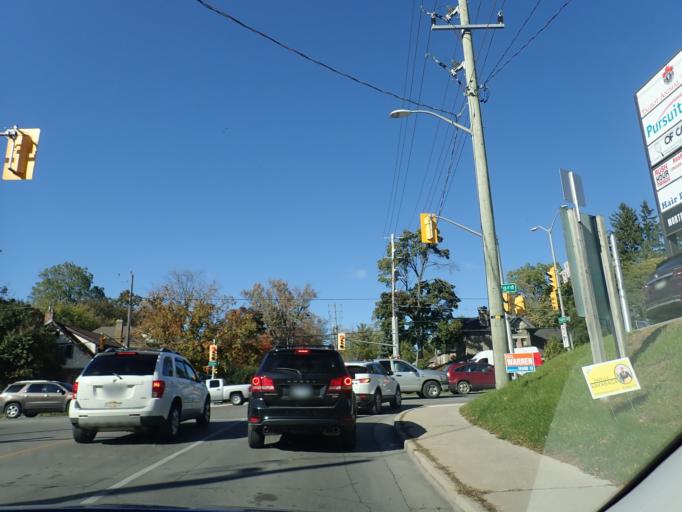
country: CA
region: Ontario
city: London
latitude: 42.9939
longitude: -81.2573
